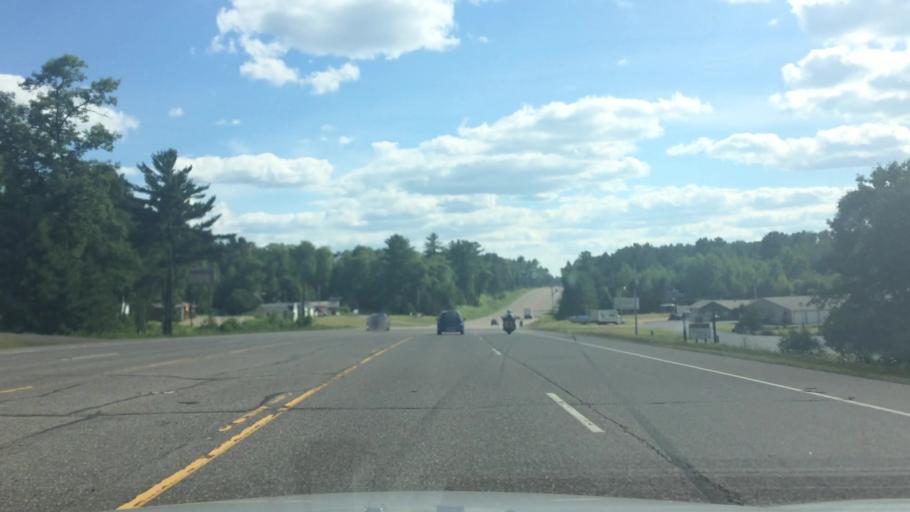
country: US
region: Wisconsin
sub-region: Vilas County
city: Lac du Flambeau
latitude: 45.8396
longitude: -89.7081
